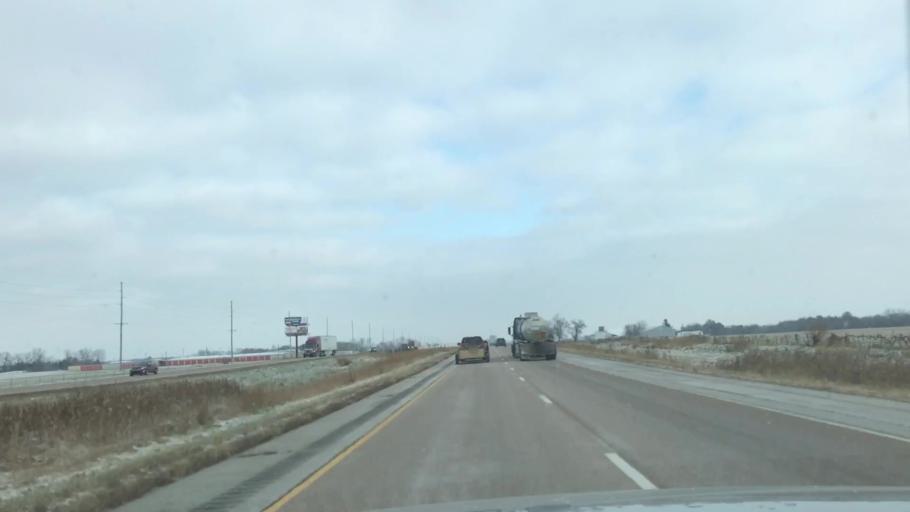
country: US
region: Illinois
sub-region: Macoupin County
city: Staunton
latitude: 39.0010
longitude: -89.7497
